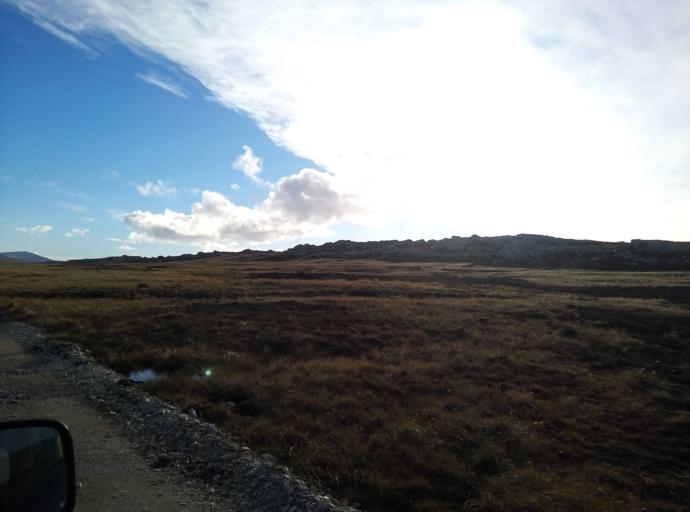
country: FK
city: Stanley
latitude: -51.6842
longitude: -57.9059
